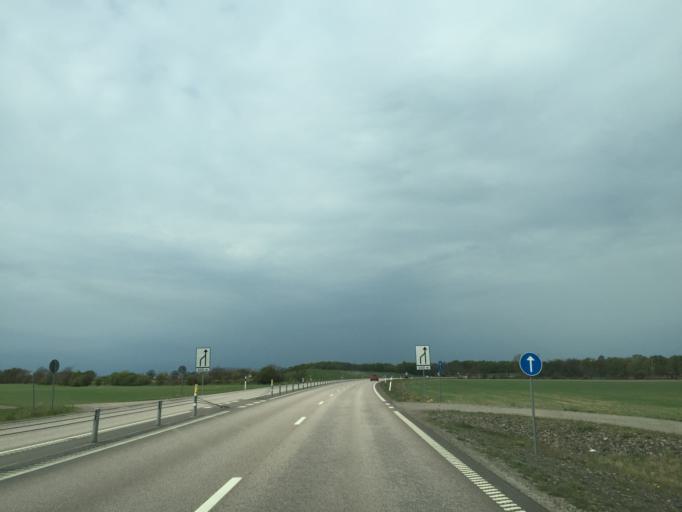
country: SE
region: Skane
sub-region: Helsingborg
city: Helsingborg
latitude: 56.0961
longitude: 12.6747
